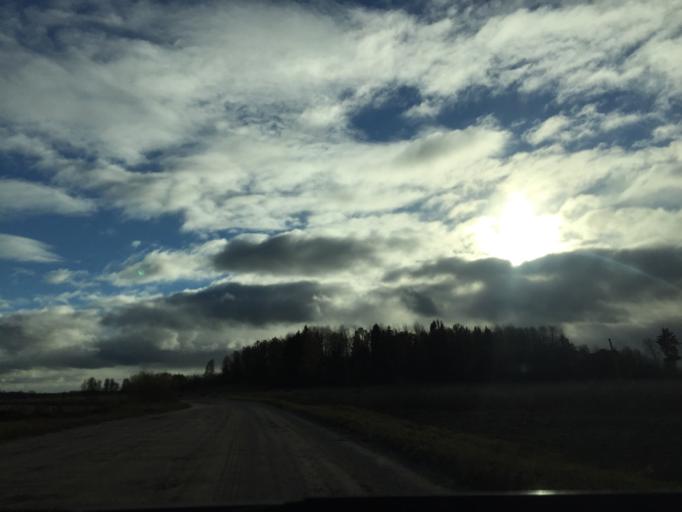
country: LV
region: Kandava
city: Kandava
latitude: 56.9491
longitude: 22.9461
